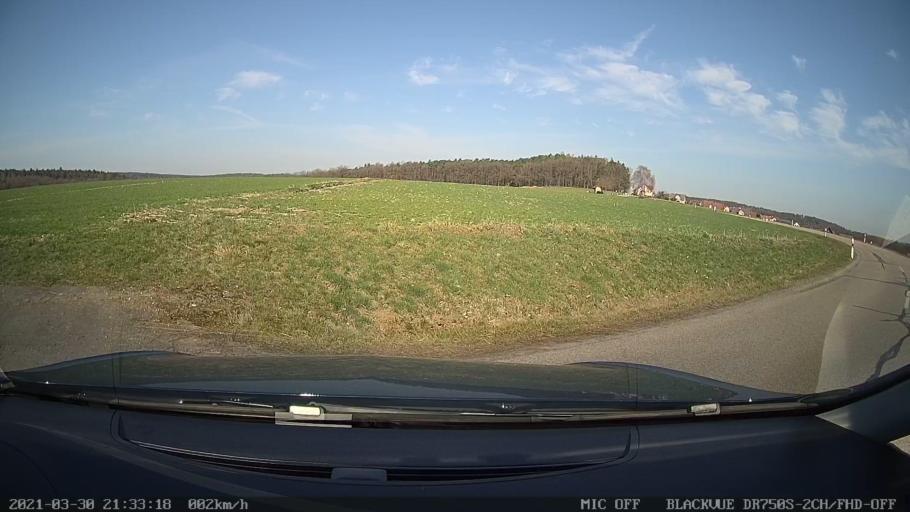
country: DE
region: Bavaria
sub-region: Upper Palatinate
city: Zeitlarn
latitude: 49.0928
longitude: 12.1041
